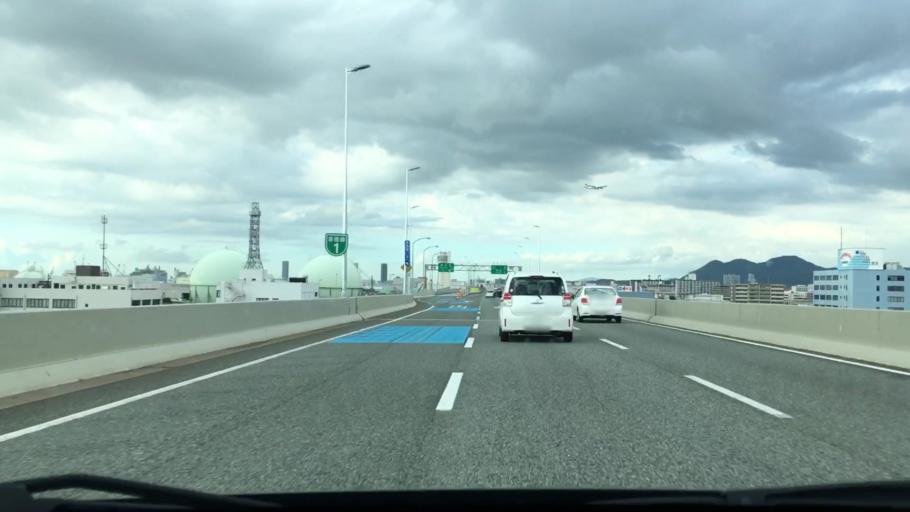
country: JP
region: Fukuoka
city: Fukuoka-shi
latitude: 33.6131
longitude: 130.4101
